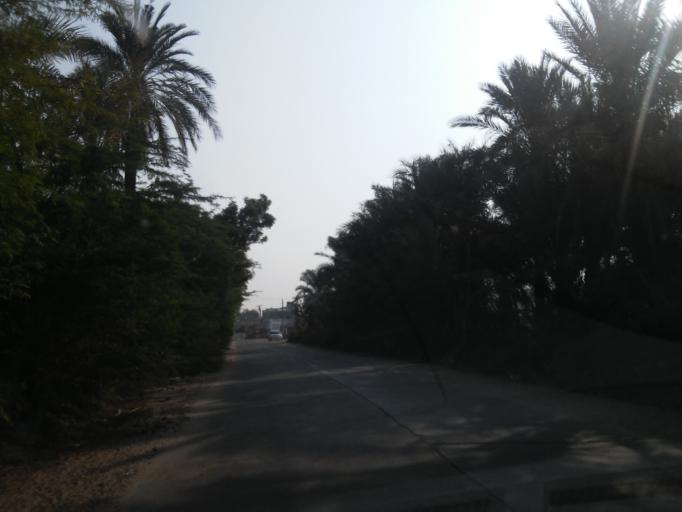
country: IN
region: Gujarat
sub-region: Kachchh
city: Mundra
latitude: 22.8344
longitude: 69.6776
